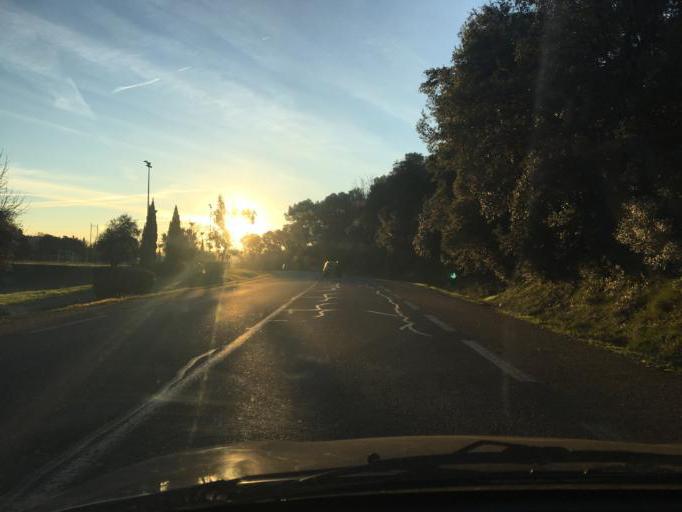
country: FR
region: Provence-Alpes-Cote d'Azur
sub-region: Departement du Var
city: Taradeau
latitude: 43.4511
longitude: 6.4308
